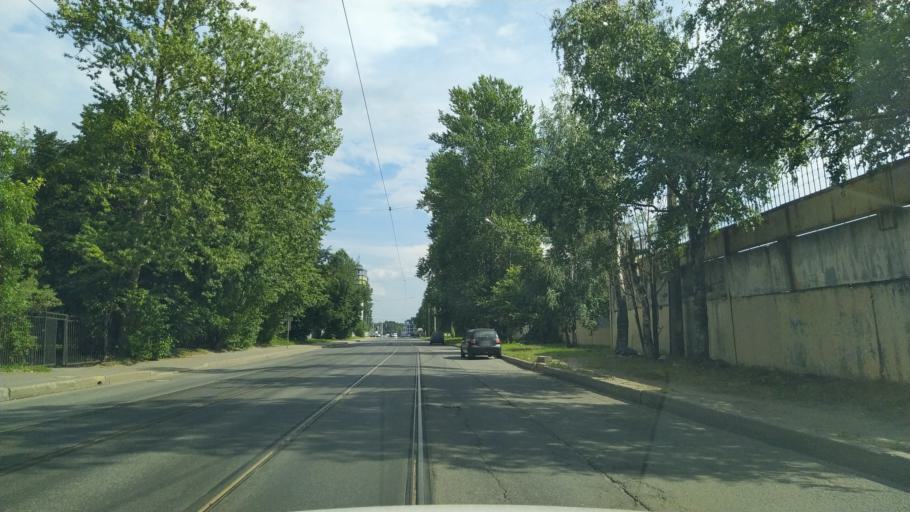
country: RU
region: Leningrad
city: Finlyandskiy
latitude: 59.9649
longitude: 30.3935
